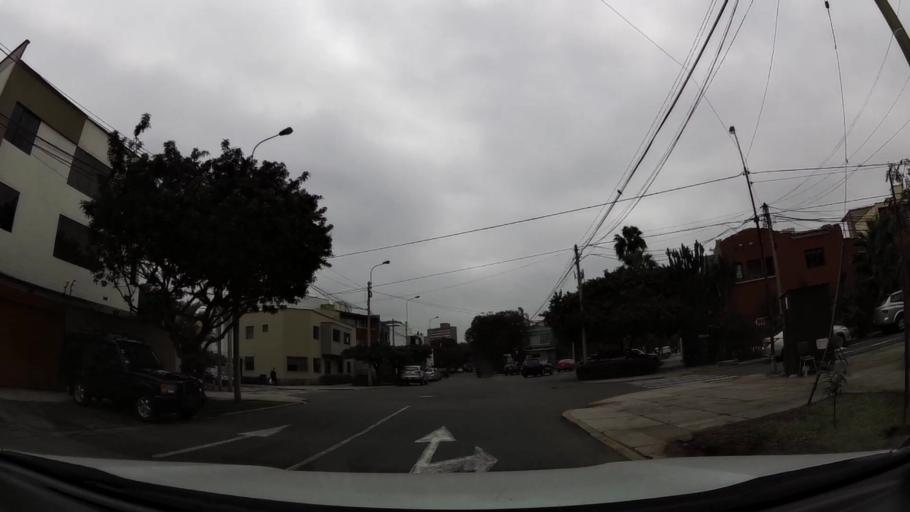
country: PE
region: Lima
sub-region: Lima
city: Surco
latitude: -12.1293
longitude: -77.0201
